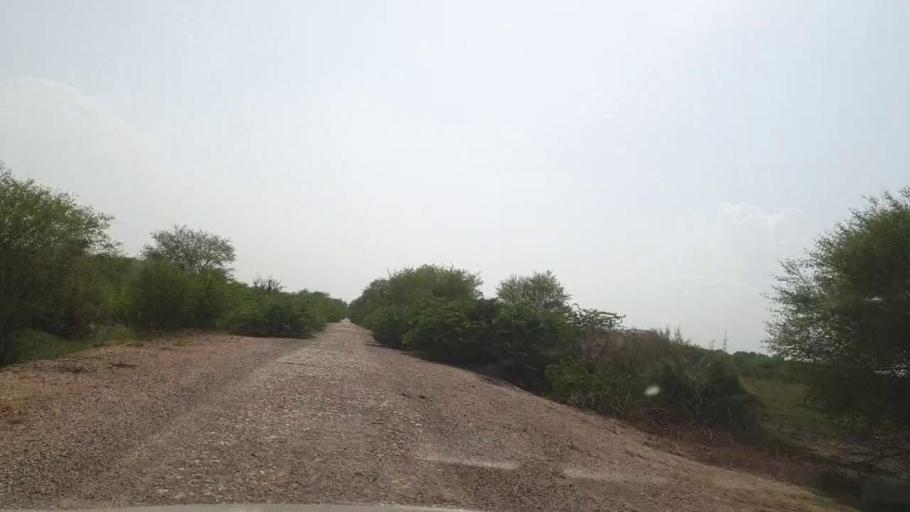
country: PK
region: Sindh
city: Pano Aqil
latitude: 27.7729
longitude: 69.1802
